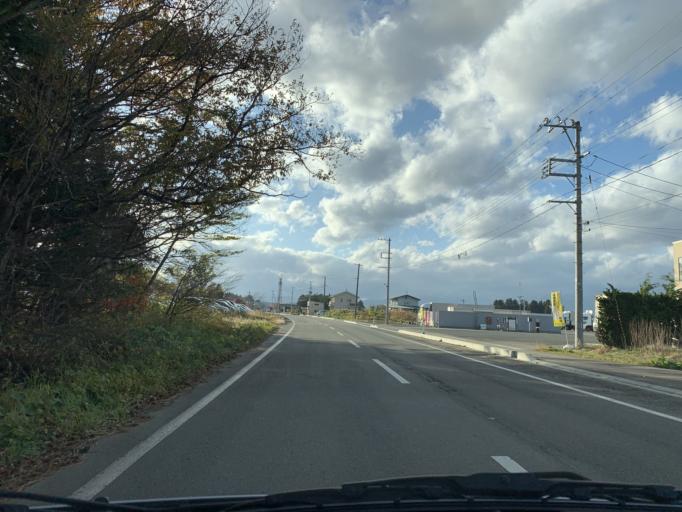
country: JP
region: Iwate
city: Mizusawa
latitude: 39.1129
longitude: 141.0732
